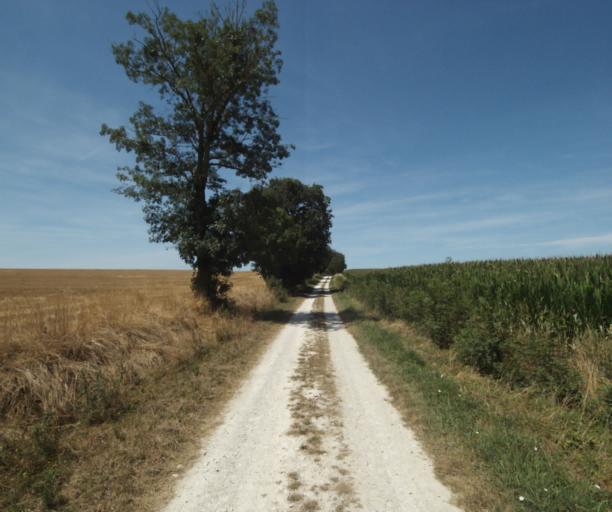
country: FR
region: Midi-Pyrenees
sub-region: Departement de la Haute-Garonne
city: Revel
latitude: 43.5042
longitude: 2.0208
